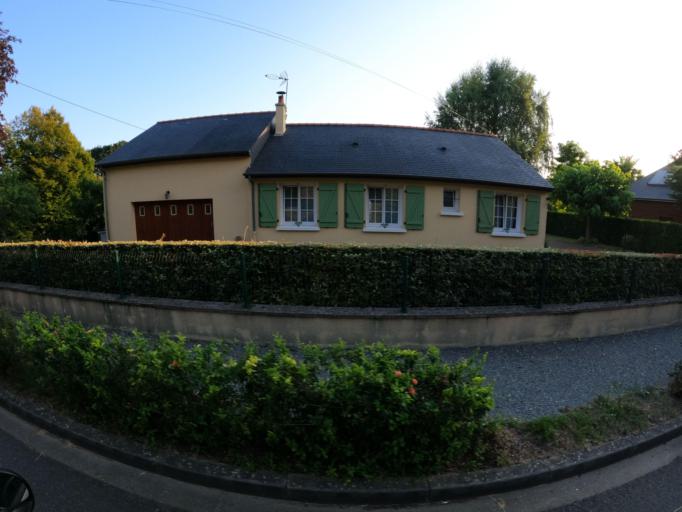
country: FR
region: Pays de la Loire
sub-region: Departement de la Sarthe
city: Parce-sur-Sarthe
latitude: 47.8627
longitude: -0.1998
